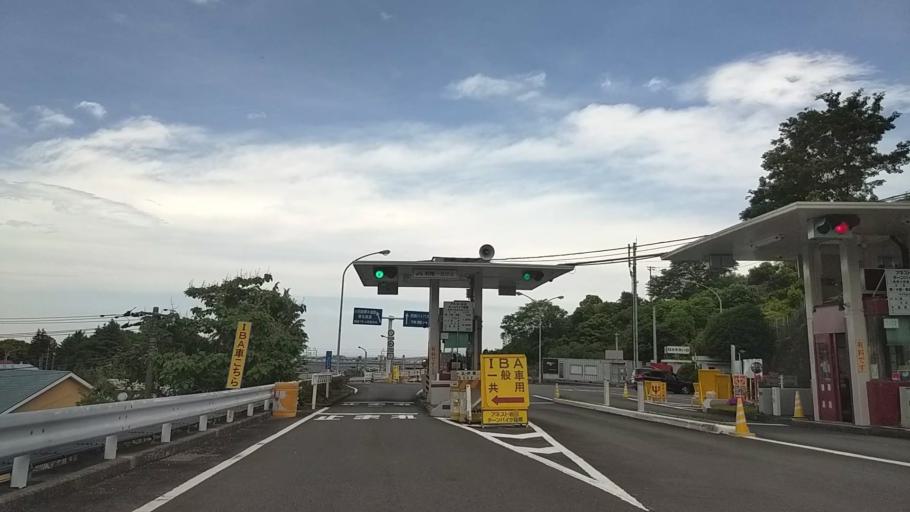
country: JP
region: Kanagawa
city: Odawara
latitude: 35.2424
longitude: 139.1404
